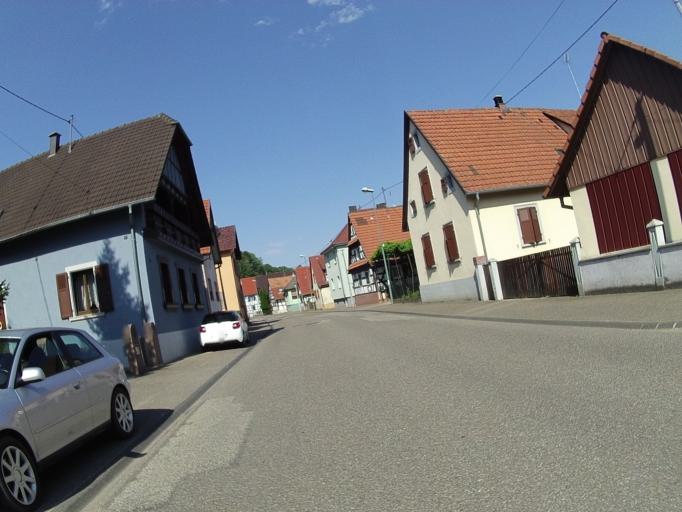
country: DE
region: Rheinland-Pfalz
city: Scheibenhardt
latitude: 48.9371
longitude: 8.1553
